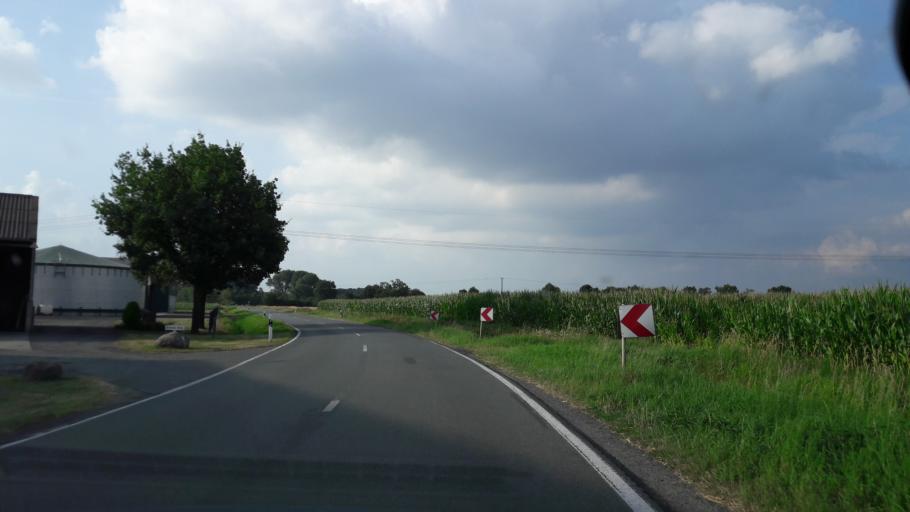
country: DE
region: North Rhine-Westphalia
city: Sendenhorst
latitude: 51.8749
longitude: 7.8094
